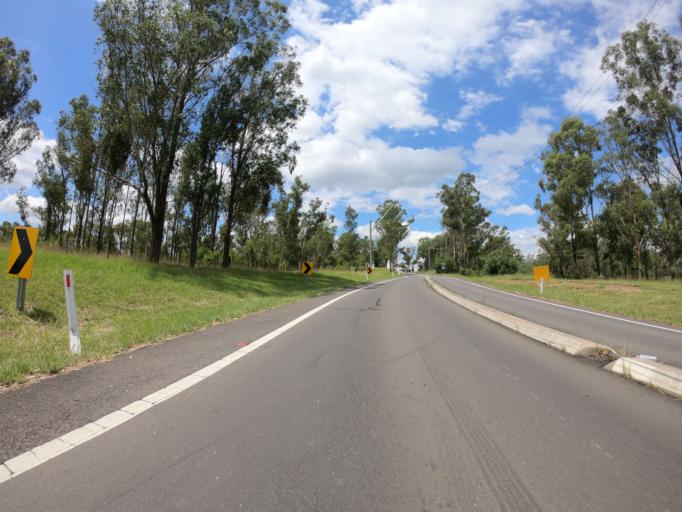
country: AU
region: New South Wales
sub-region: Penrith Municipality
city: Mulgoa
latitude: -33.8272
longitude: 150.6654
